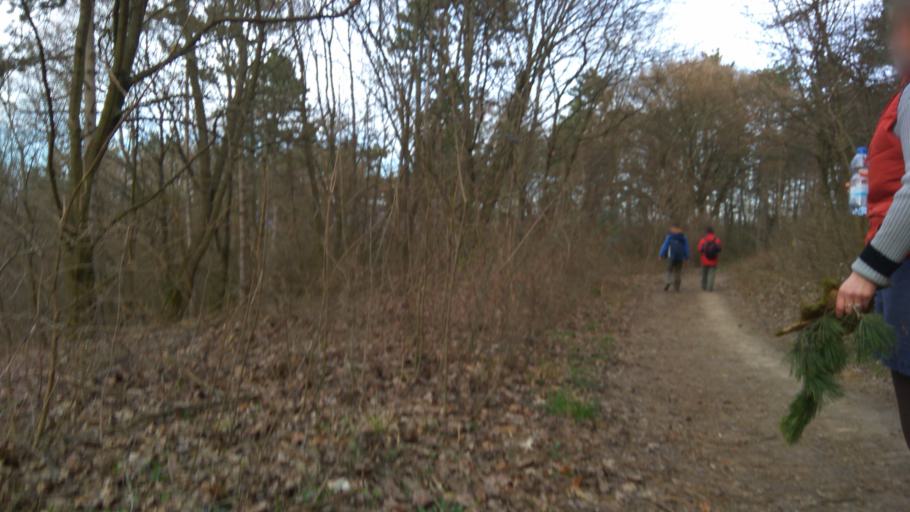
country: HU
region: Pest
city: Pilisborosjeno
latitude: 47.6217
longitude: 19.0090
